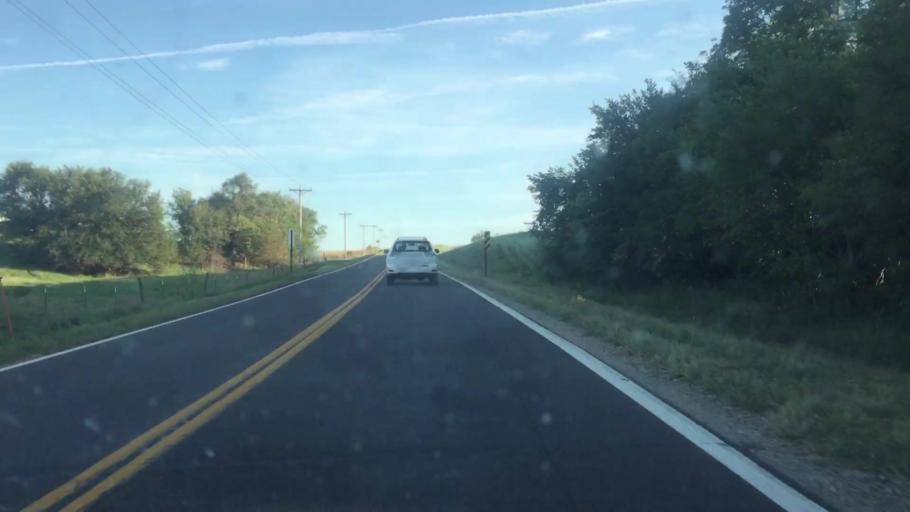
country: US
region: Kansas
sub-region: Brown County
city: Horton
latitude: 39.5693
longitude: -95.5267
